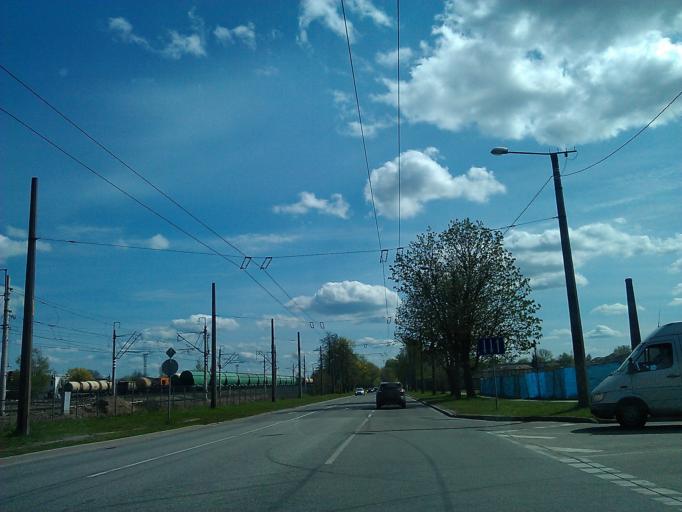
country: LV
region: Riga
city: Riga
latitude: 56.9268
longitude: 24.1752
